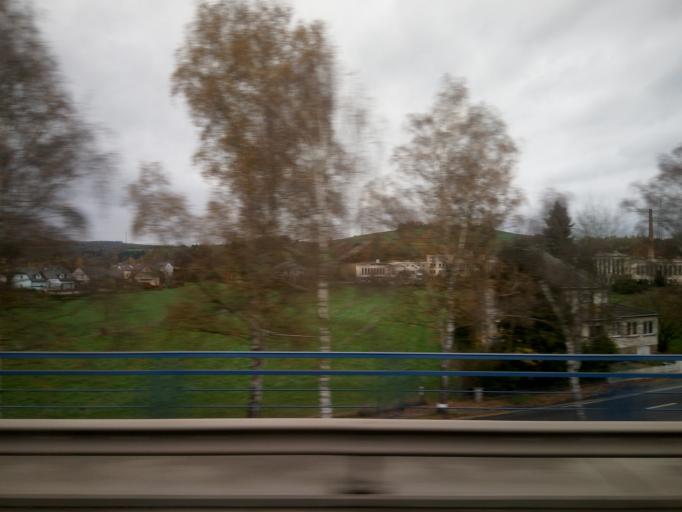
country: LU
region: Diekirch
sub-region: Canton de Diekirch
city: Ettelbruck
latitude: 49.8501
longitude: 6.1165
